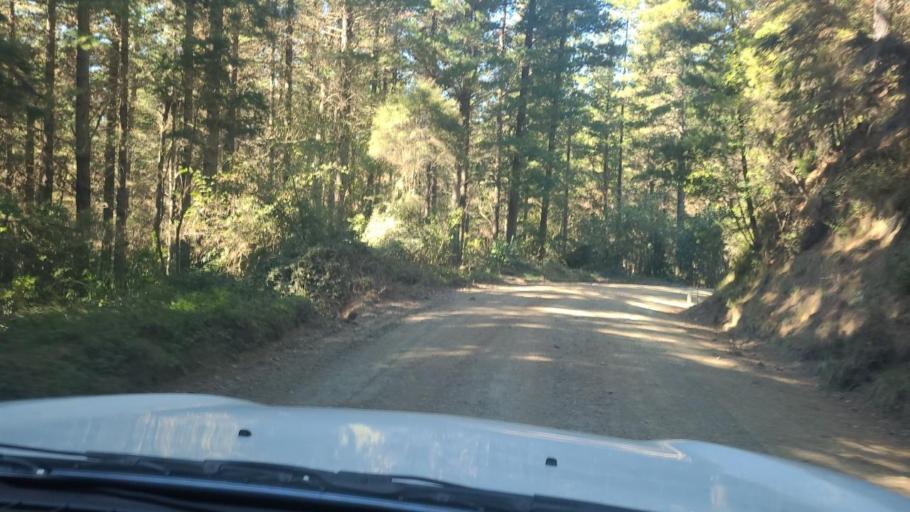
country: NZ
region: Hawke's Bay
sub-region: Napier City
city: Taradale
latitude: -39.4109
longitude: 176.4858
